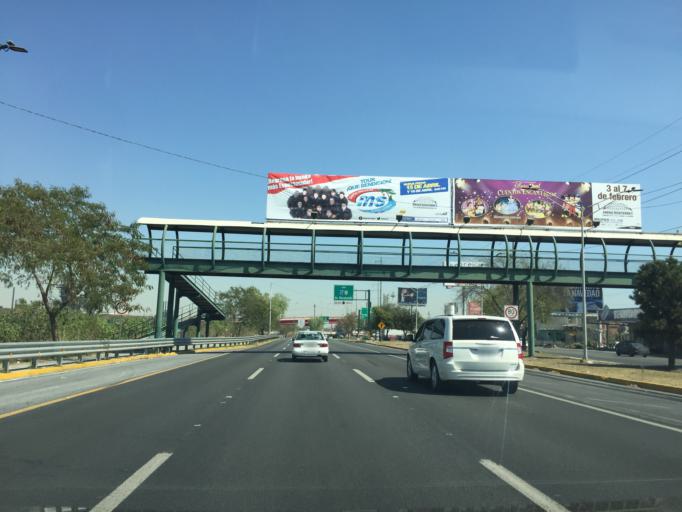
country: MX
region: Nuevo Leon
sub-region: Monterrey
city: Monterrey
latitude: 25.6703
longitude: -100.2893
